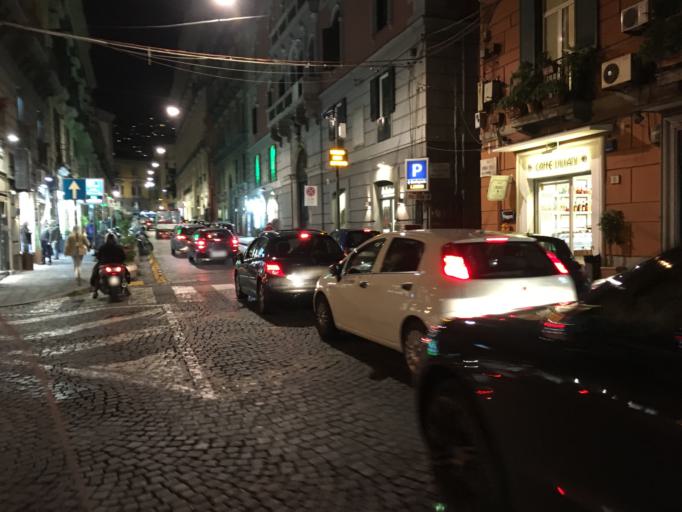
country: IT
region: Campania
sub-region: Provincia di Napoli
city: Napoli
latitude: 40.8329
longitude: 14.2429
